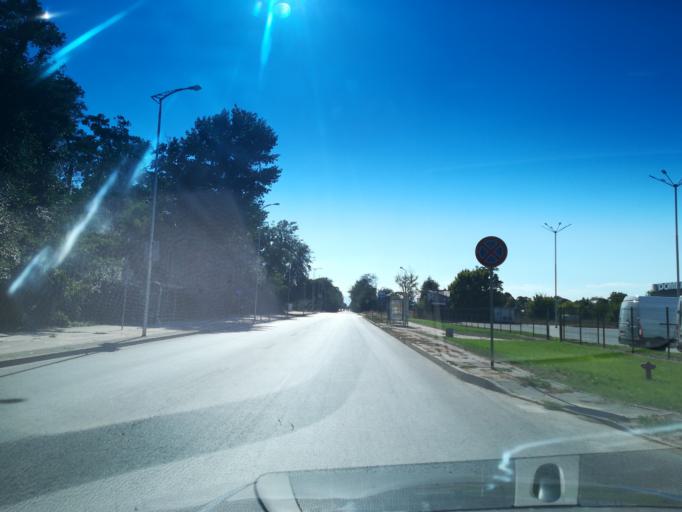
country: BG
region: Plovdiv
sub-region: Obshtina Plovdiv
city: Plovdiv
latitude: 42.1550
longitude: 24.7076
